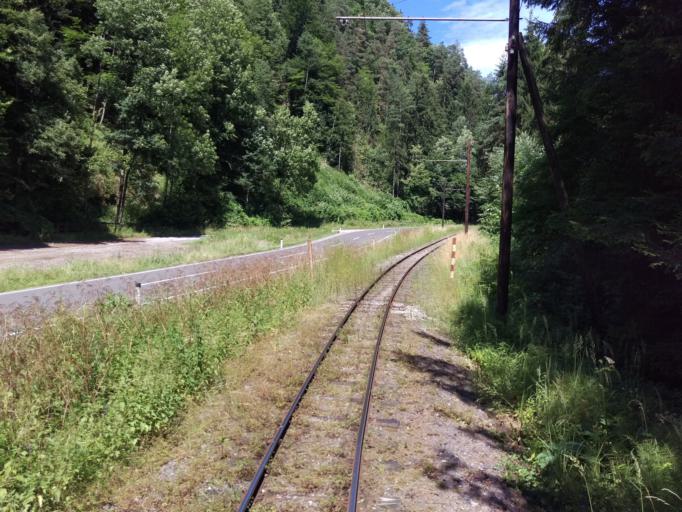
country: AT
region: Styria
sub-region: Politischer Bezirk Bruck-Muerzzuschlag
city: Pernegg an der Mur
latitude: 47.3629
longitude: 15.3766
